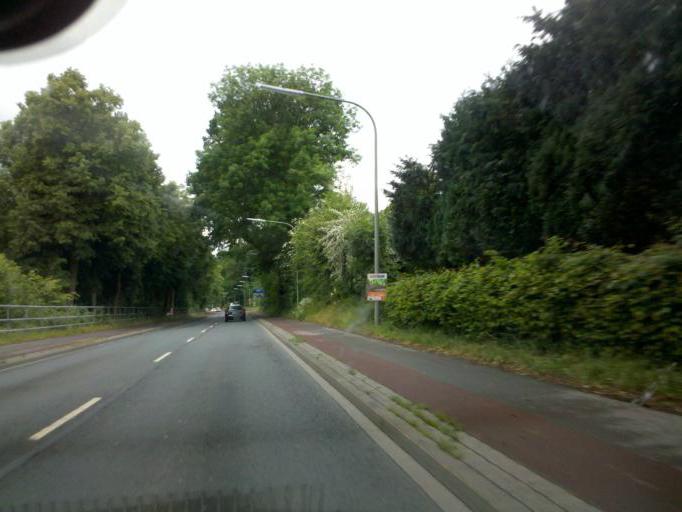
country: DE
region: North Rhine-Westphalia
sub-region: Regierungsbezirk Arnsberg
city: Meschede
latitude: 51.3562
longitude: 8.2839
